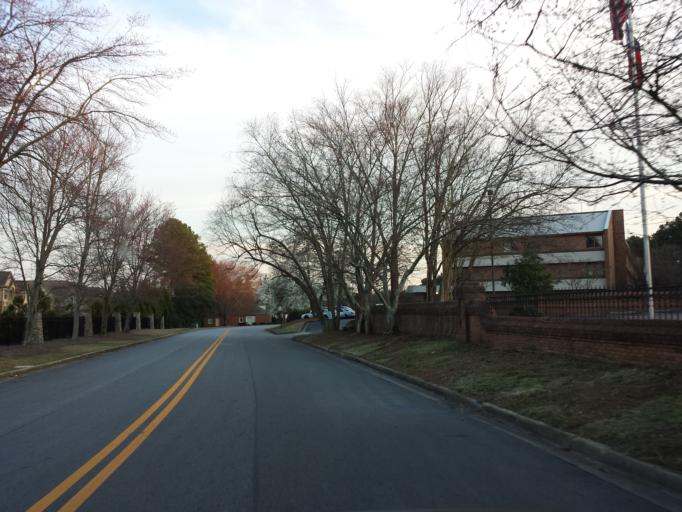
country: US
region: Georgia
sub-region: Cobb County
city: Vinings
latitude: 33.9075
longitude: -84.4748
